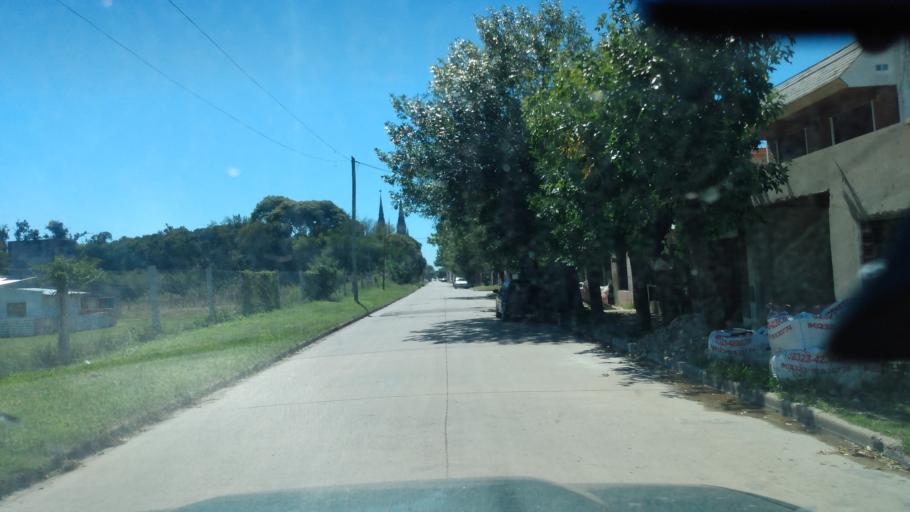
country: AR
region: Buenos Aires
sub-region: Partido de Lujan
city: Lujan
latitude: -34.5714
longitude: -59.1238
